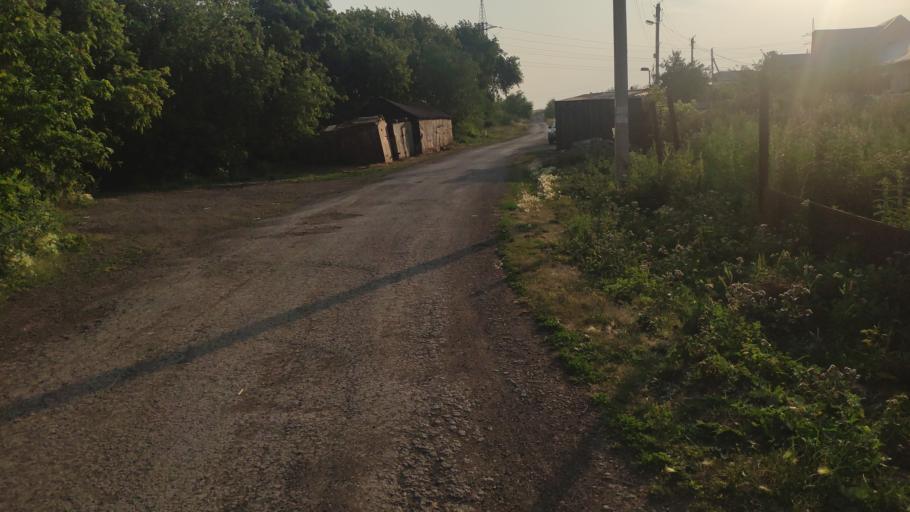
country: RU
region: Chelyabinsk
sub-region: Gorod Magnitogorsk
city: Magnitogorsk
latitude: 53.3731
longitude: 59.0606
